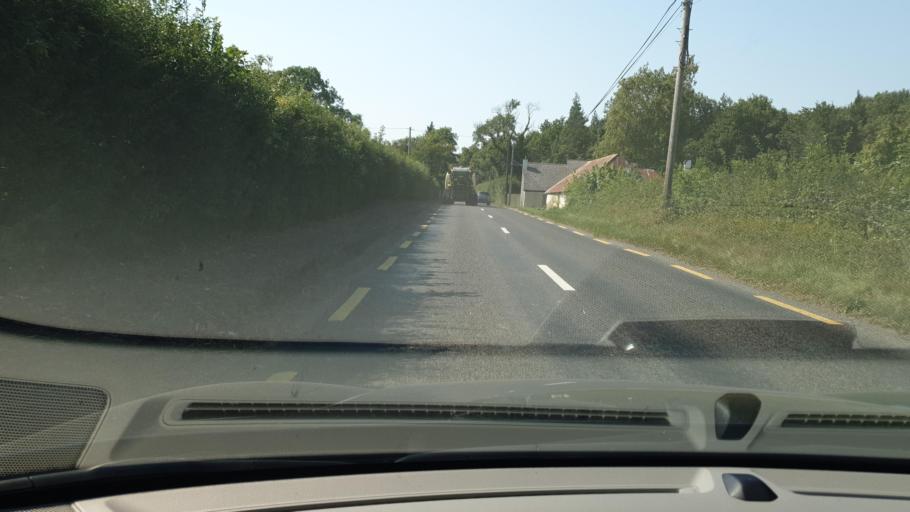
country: IE
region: Leinster
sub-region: An Mhi
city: Trim
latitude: 53.5800
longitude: -6.8422
